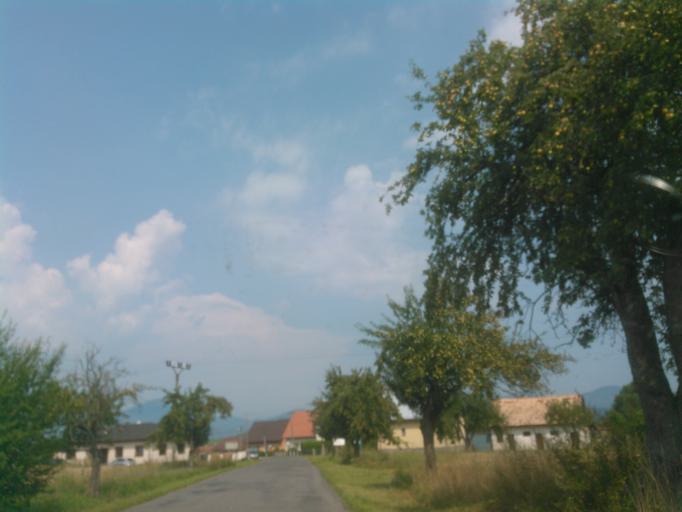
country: SK
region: Zilinsky
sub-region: Okres Liptovsky Mikulas
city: Liptovsky Mikulas
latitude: 49.0482
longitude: 19.4861
